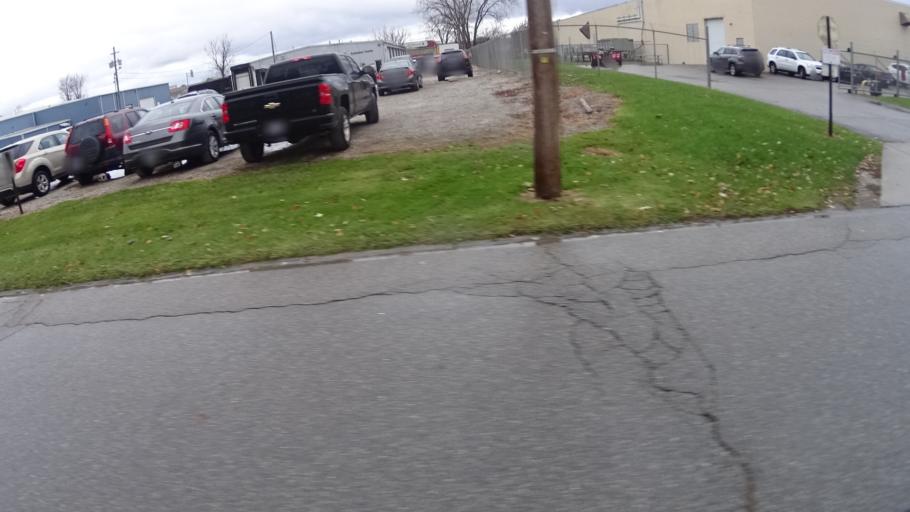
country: US
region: Ohio
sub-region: Lorain County
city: Elyria
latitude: 41.3891
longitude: -82.1225
